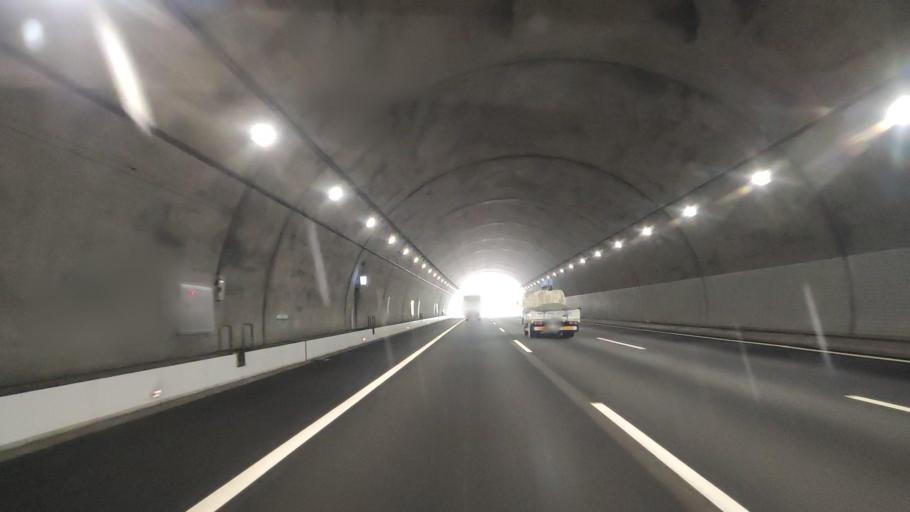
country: JP
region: Shizuoka
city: Shizuoka-shi
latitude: 35.0523
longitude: 138.4191
